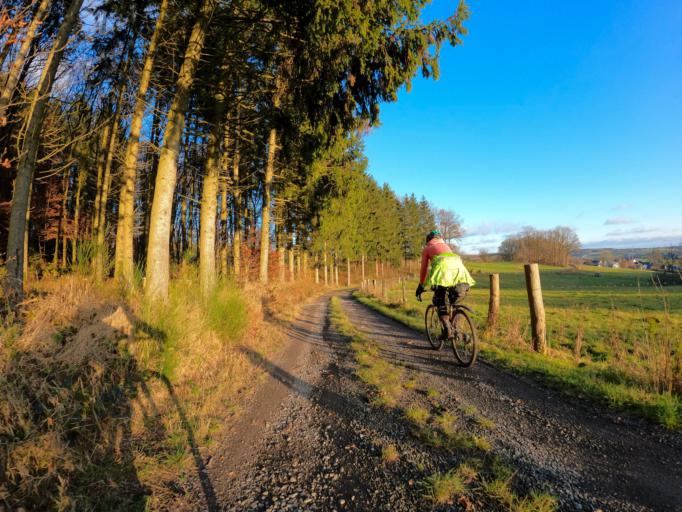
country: LU
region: Diekirch
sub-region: Canton de Wiltz
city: Bavigne
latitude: 49.9718
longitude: 5.8294
